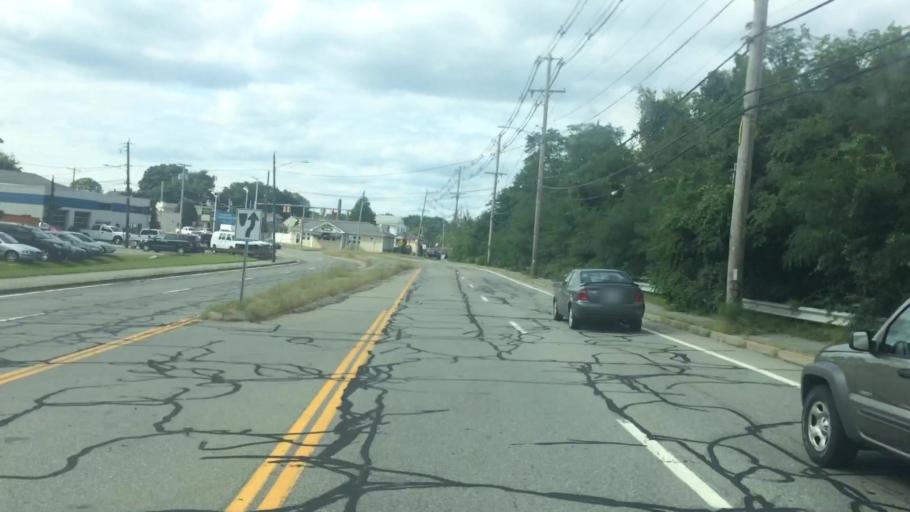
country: US
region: Rhode Island
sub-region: Providence County
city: Cranston
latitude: 41.7921
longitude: -71.4725
